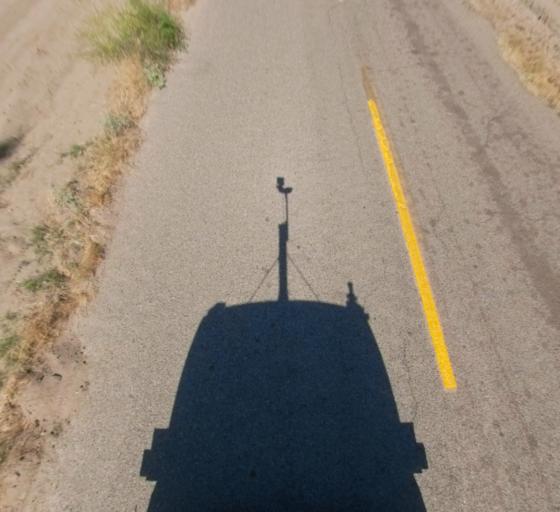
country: US
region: California
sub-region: Fresno County
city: Biola
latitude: 36.8368
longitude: -120.0026
